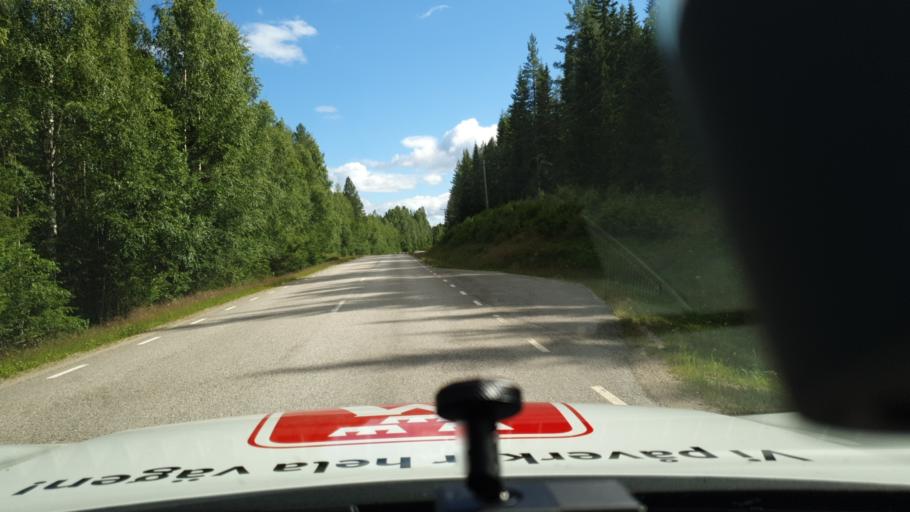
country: NO
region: Hedmark
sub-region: Trysil
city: Innbygda
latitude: 61.0105
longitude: 12.4799
